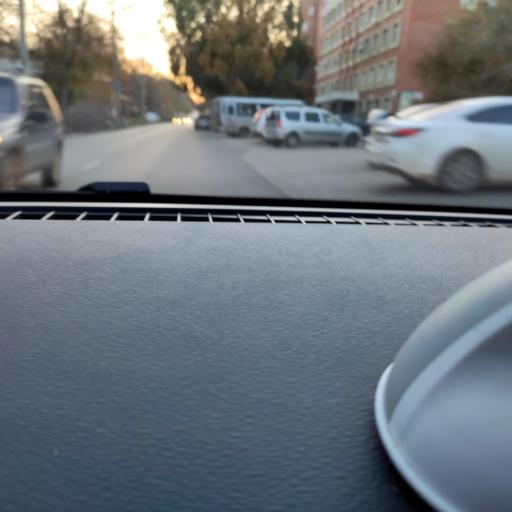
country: RU
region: Samara
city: Samara
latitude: 53.2237
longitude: 50.2300
